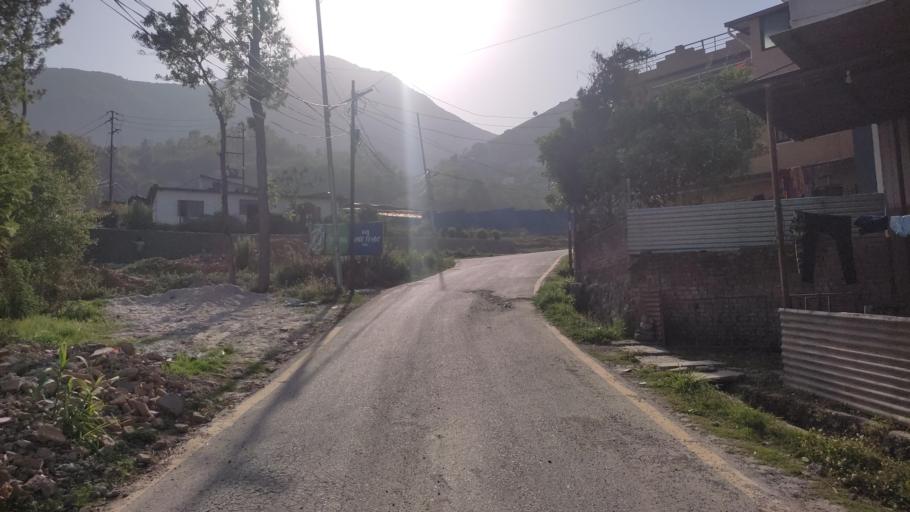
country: NP
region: Central Region
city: Kirtipur
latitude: 27.6499
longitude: 85.2782
